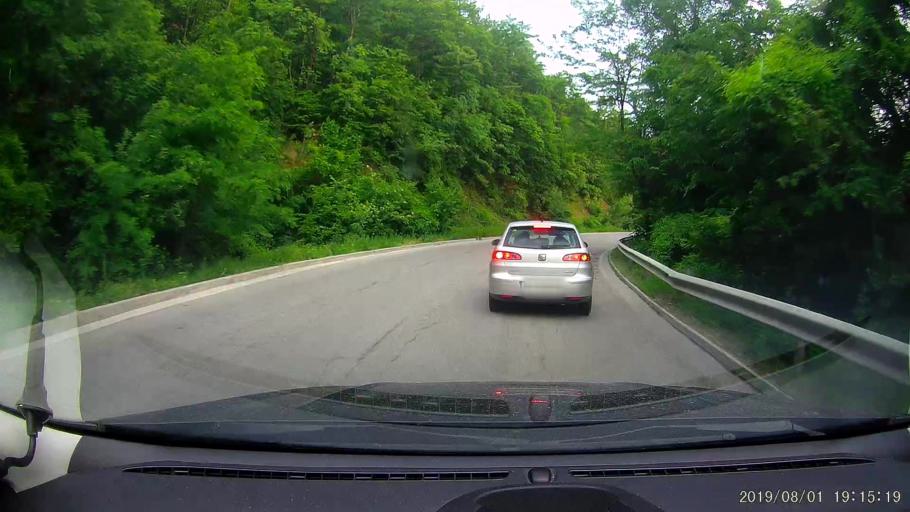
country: BG
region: Shumen
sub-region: Obshtina Smyadovo
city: Smyadovo
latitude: 42.9337
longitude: 26.9440
